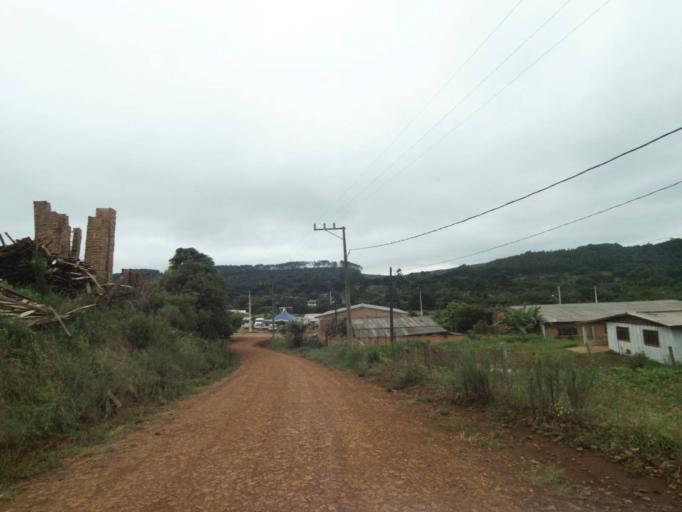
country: BR
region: Parana
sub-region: Pitanga
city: Pitanga
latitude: -24.9320
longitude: -51.8744
